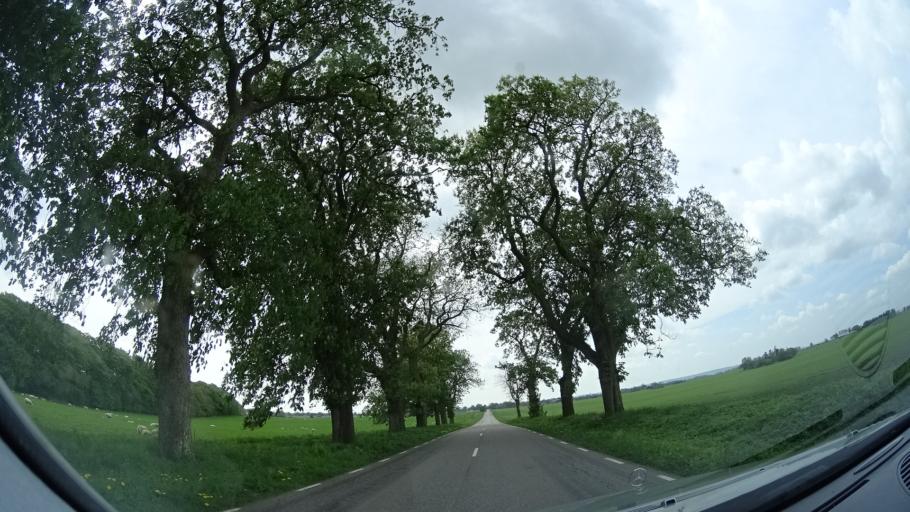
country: SE
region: Skane
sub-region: Hoors Kommun
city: Loberod
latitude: 55.7701
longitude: 13.4830
